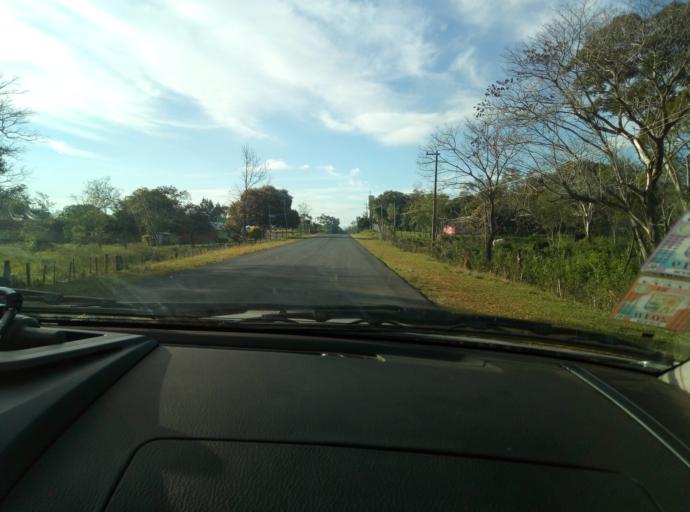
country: PY
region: Caaguazu
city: Carayao
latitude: -25.1601
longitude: -56.3121
